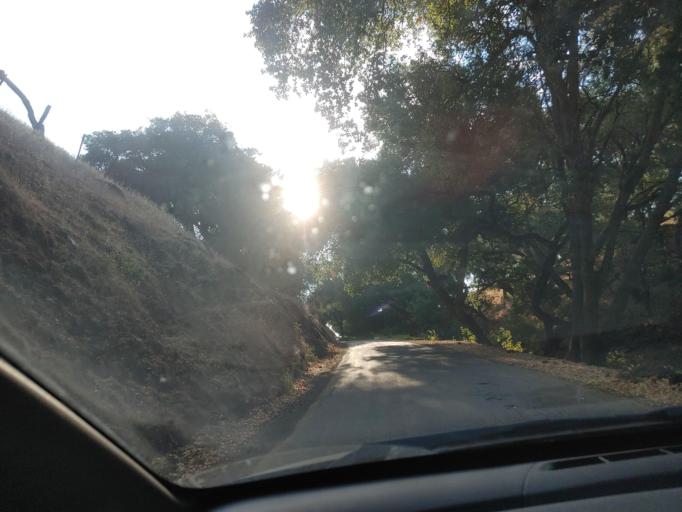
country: US
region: California
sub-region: San Benito County
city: Ridgemark
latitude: 36.7686
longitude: -121.1981
